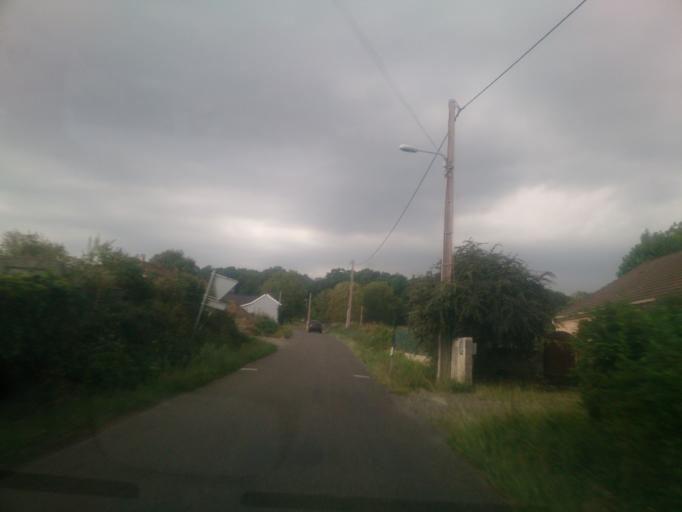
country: FR
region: Midi-Pyrenees
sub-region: Departement des Hautes-Pyrenees
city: Horgues
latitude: 43.1499
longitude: 0.0860
